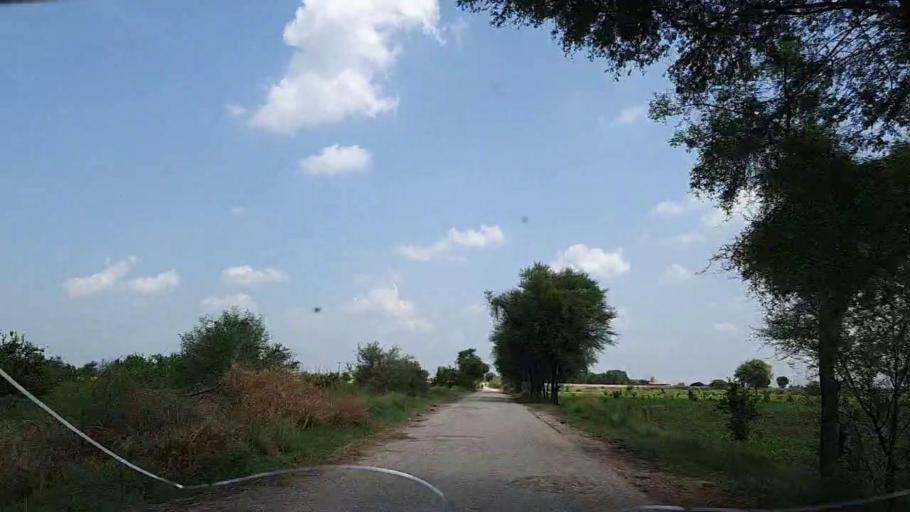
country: PK
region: Sindh
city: Tharu Shah
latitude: 26.9968
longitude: 68.0689
